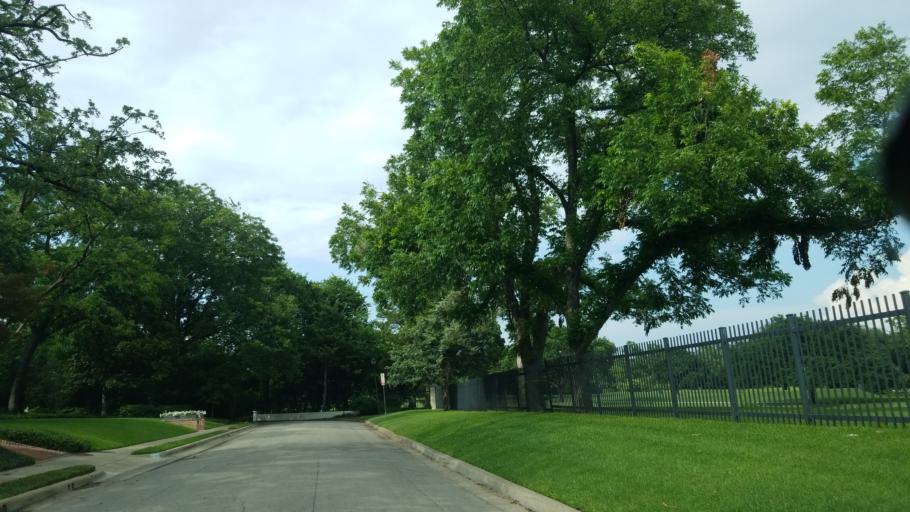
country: US
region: Texas
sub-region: Dallas County
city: Highland Park
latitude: 32.8389
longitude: -96.8018
